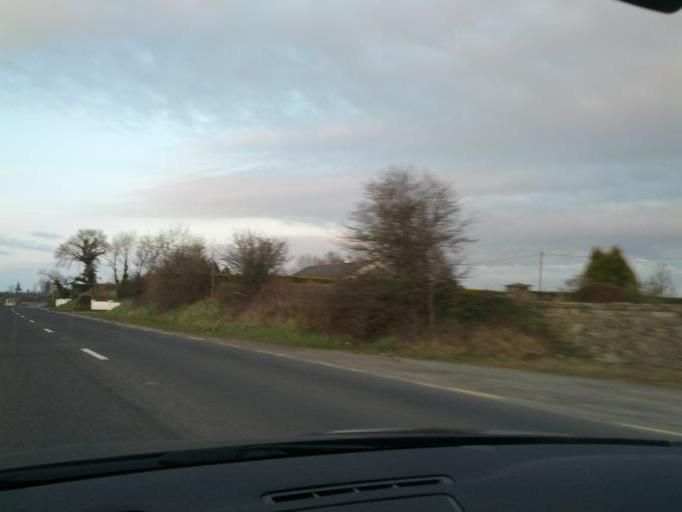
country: IE
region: Munster
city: Nenagh Bridge
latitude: 52.9105
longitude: -8.1802
